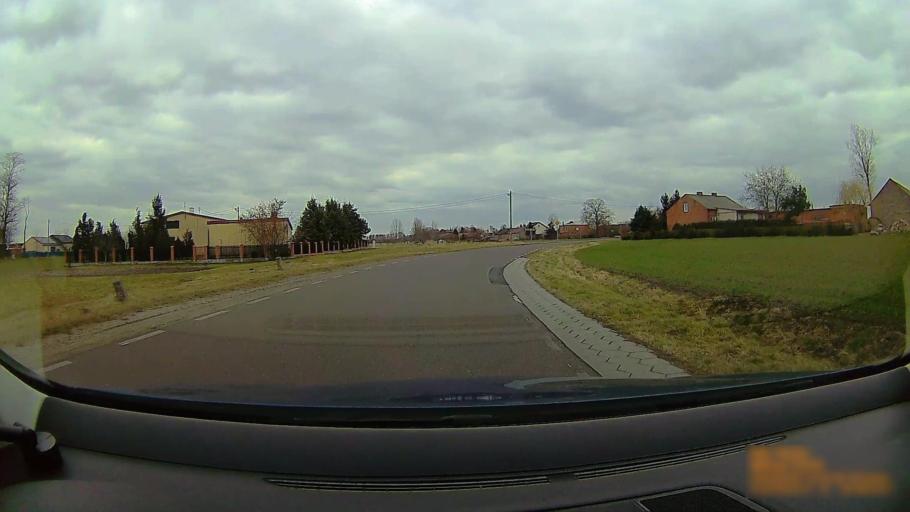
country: PL
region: Greater Poland Voivodeship
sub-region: Powiat koninski
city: Rzgow Pierwszy
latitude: 52.1061
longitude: 18.0849
